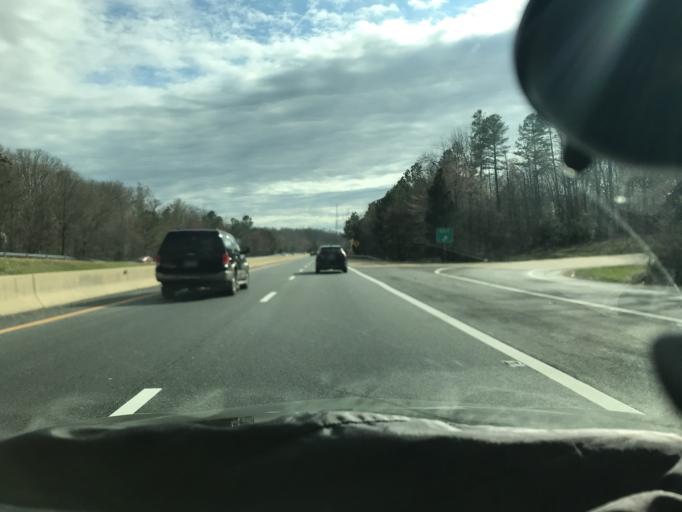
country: US
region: Virginia
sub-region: Chesterfield County
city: Bon Air
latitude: 37.5182
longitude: -77.5348
